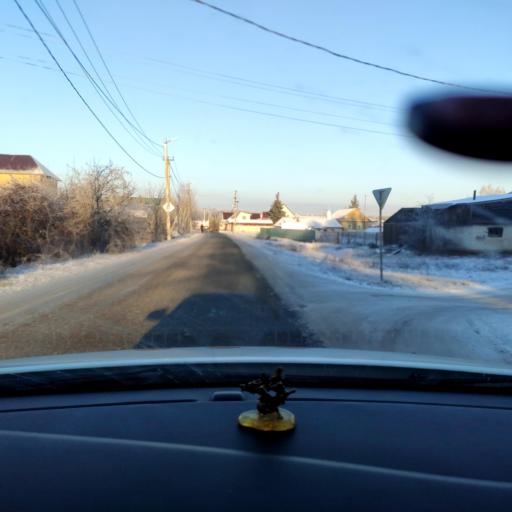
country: RU
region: Tatarstan
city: Stolbishchi
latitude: 55.6747
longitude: 49.1178
